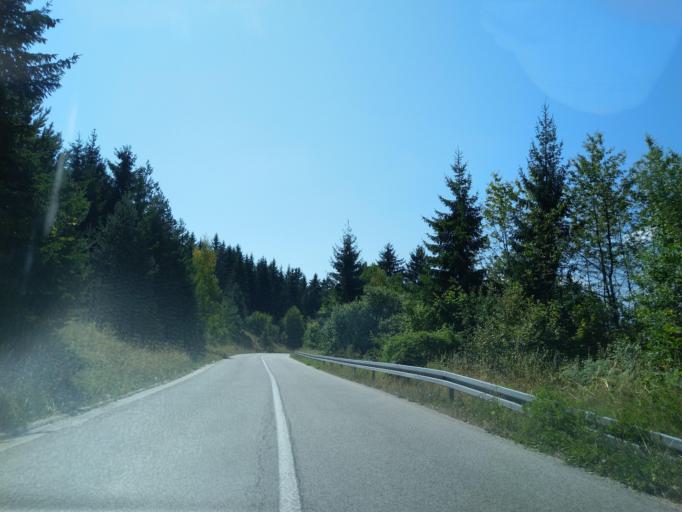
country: RS
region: Central Serbia
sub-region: Zlatiborski Okrug
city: Nova Varos
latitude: 43.3509
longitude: 19.8531
